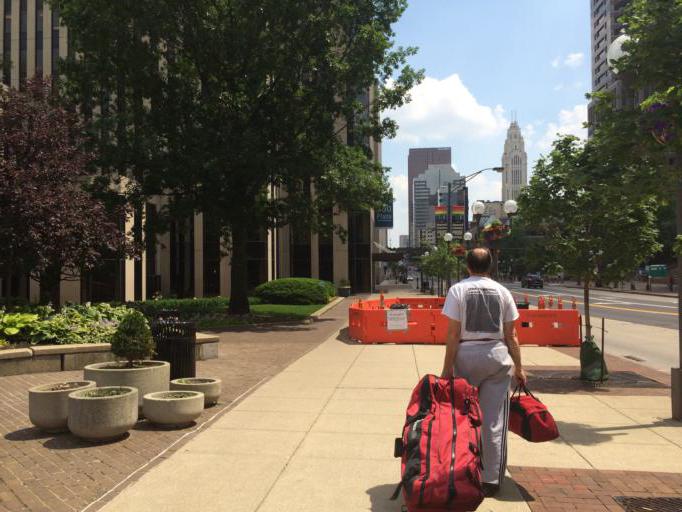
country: US
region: Ohio
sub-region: Franklin County
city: Columbus
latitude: 39.9685
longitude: -83.0017
